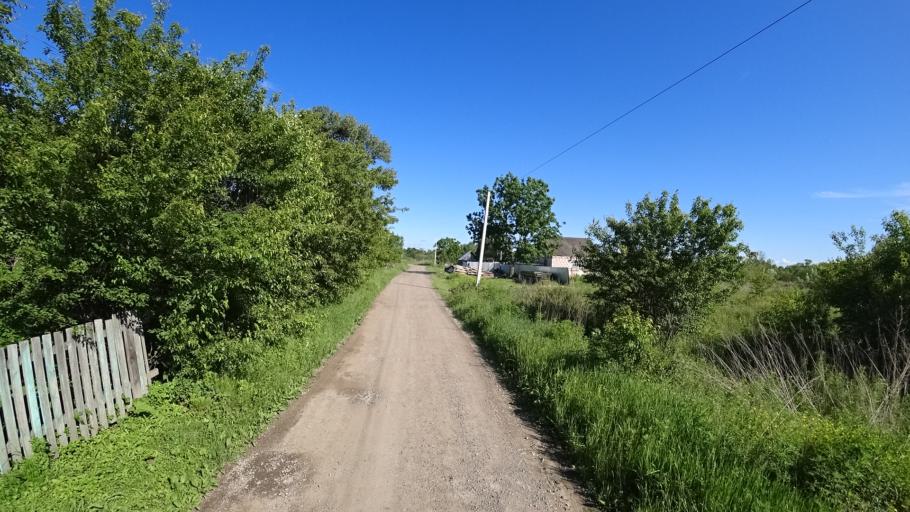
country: RU
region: Khabarovsk Krai
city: Khor
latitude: 47.8848
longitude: 135.0190
